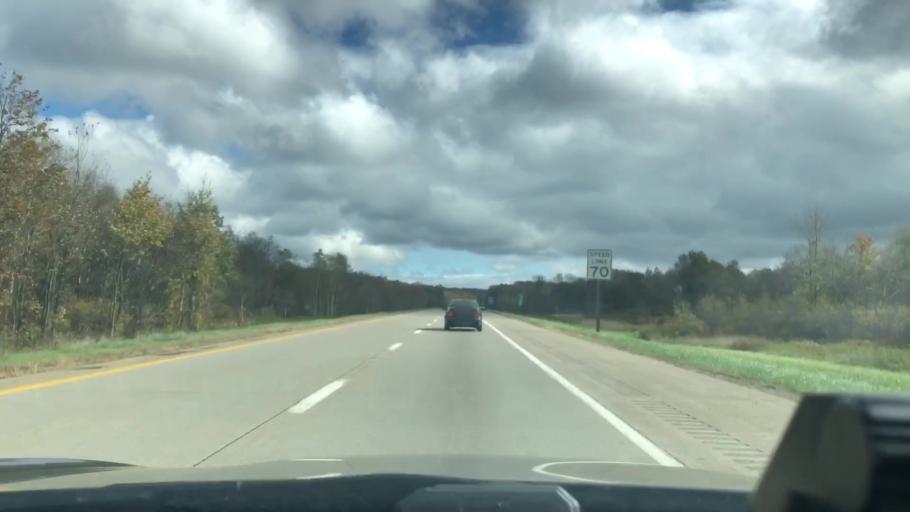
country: US
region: Pennsylvania
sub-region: Lackawanna County
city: Moscow
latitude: 41.2251
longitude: -75.4897
